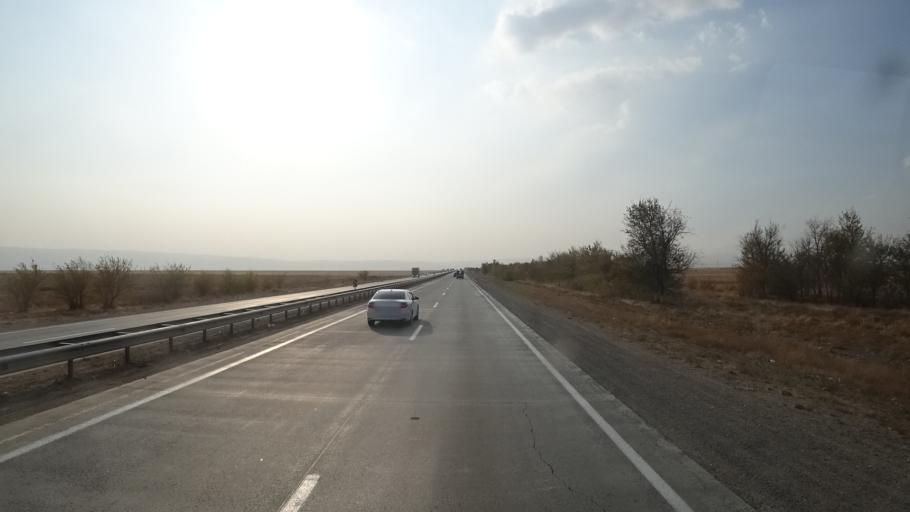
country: KZ
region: Zhambyl
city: Taraz
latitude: 42.8096
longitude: 71.1239
